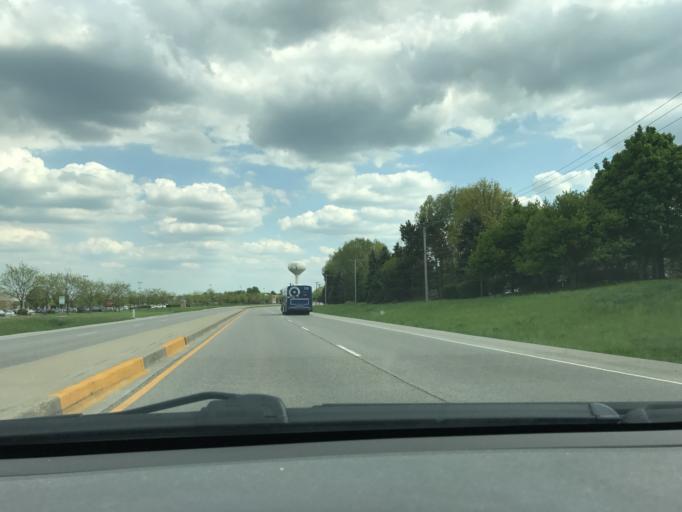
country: US
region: Illinois
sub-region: Kane County
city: South Elgin
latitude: 42.0198
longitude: -88.3382
